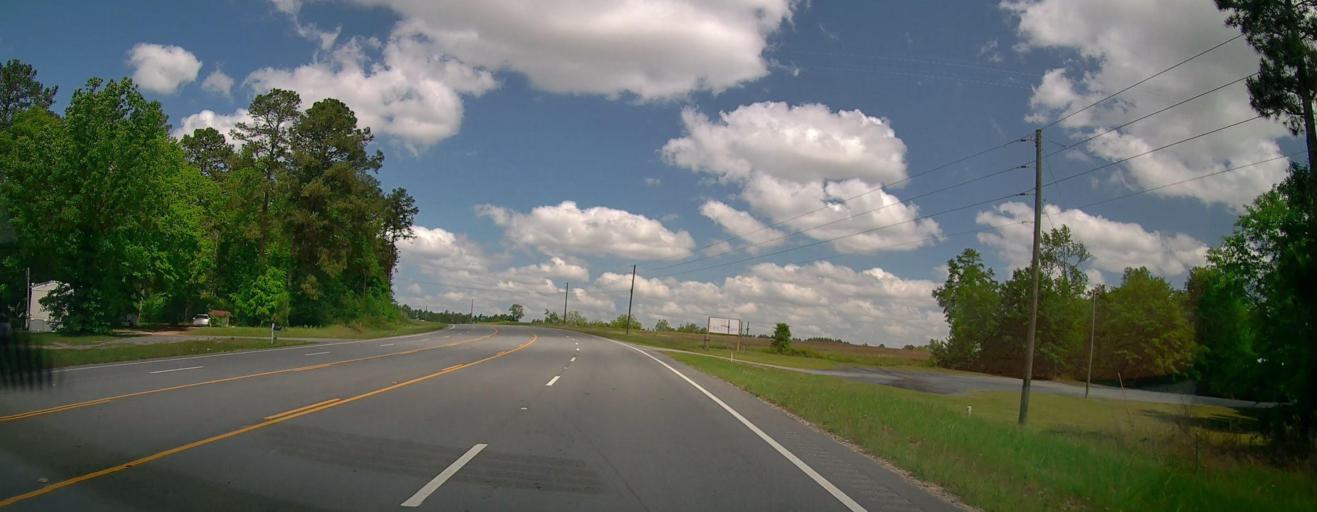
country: US
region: Georgia
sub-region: Bleckley County
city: Cochran
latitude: 32.3937
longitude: -83.3243
